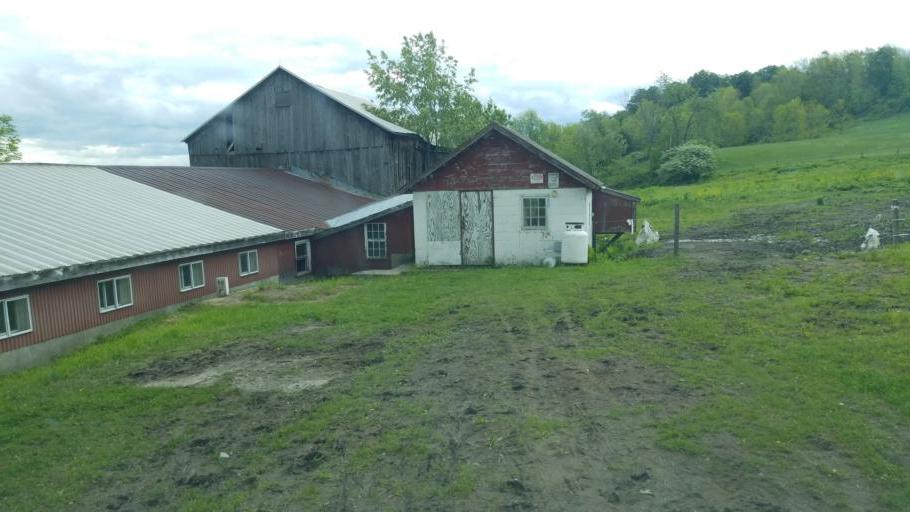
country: US
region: New York
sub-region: Otsego County
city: Richfield Springs
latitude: 42.8450
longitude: -75.1554
